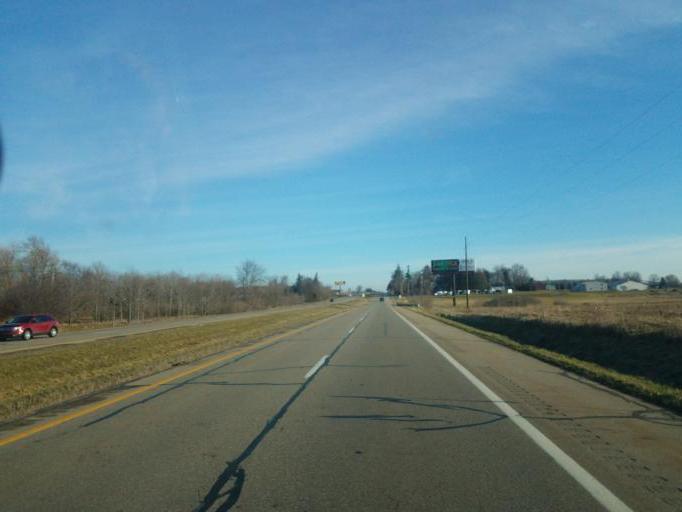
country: US
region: Michigan
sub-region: Clinton County
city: Saint Johns
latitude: 43.0554
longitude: -84.5637
